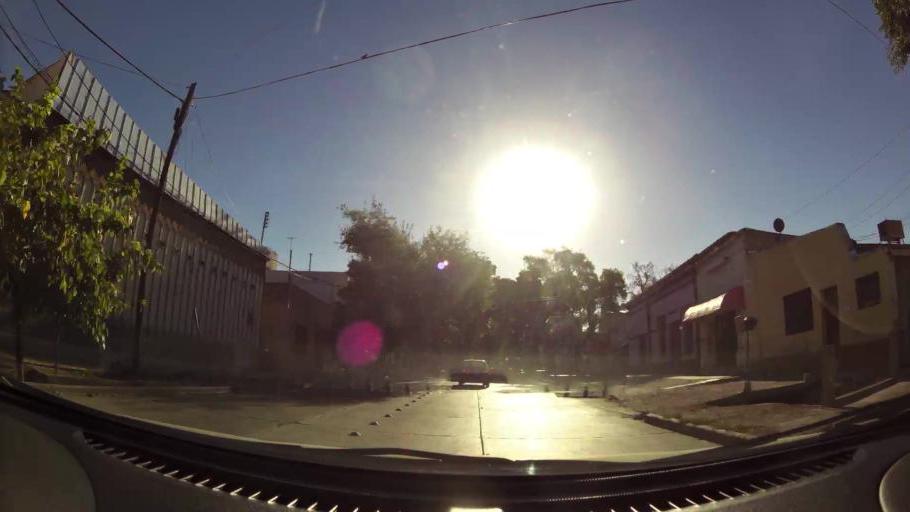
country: AR
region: Mendoza
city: Las Heras
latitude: -32.8667
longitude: -68.8326
